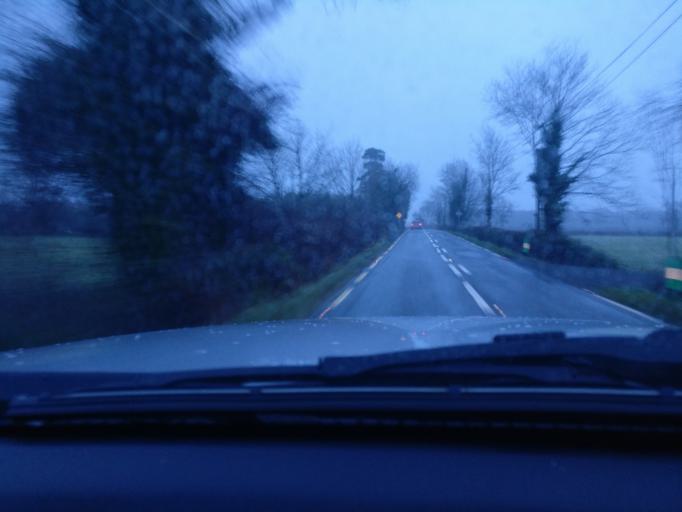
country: IE
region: Leinster
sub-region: An Mhi
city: Athboy
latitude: 53.6390
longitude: -6.8313
